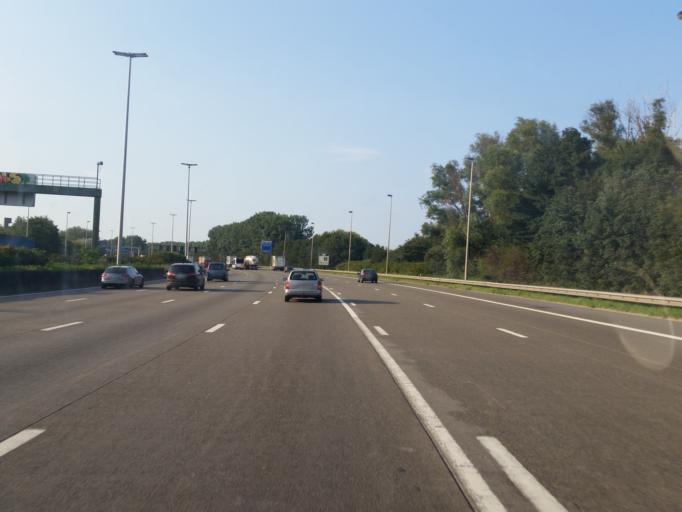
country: BE
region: Flanders
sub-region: Provincie Antwerpen
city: Borsbeek
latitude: 51.2212
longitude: 4.4511
